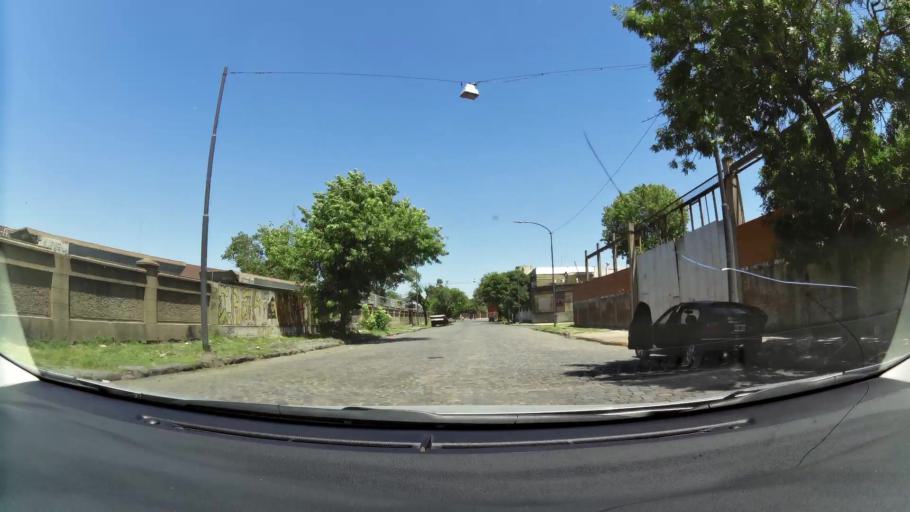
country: AR
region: Buenos Aires
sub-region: Partido de Avellaneda
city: Avellaneda
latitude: -34.6446
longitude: -58.3878
